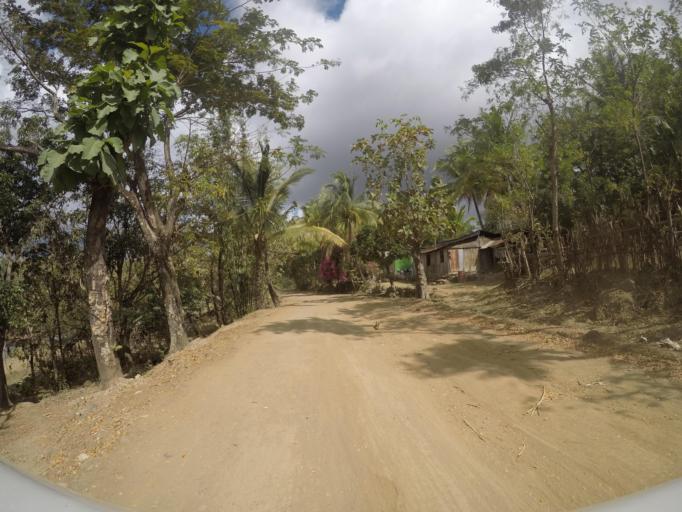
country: TL
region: Lautem
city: Lospalos
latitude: -8.5460
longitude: 126.8351
